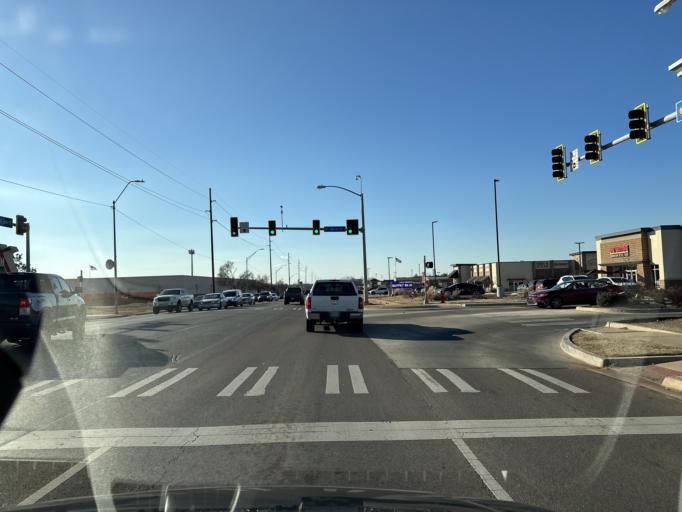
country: US
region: Oklahoma
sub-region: Oklahoma County
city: Midwest City
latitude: 35.4498
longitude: -97.4191
